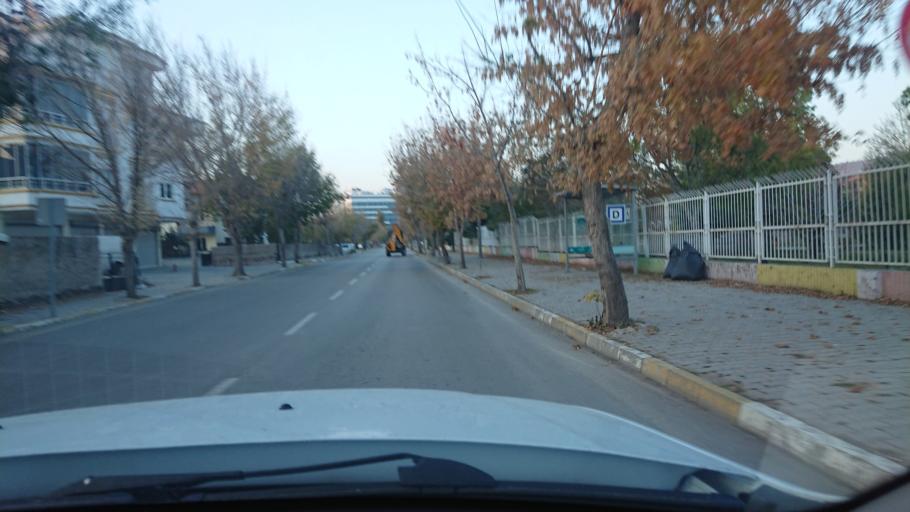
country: TR
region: Aksaray
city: Aksaray
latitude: 38.3551
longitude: 34.0419
